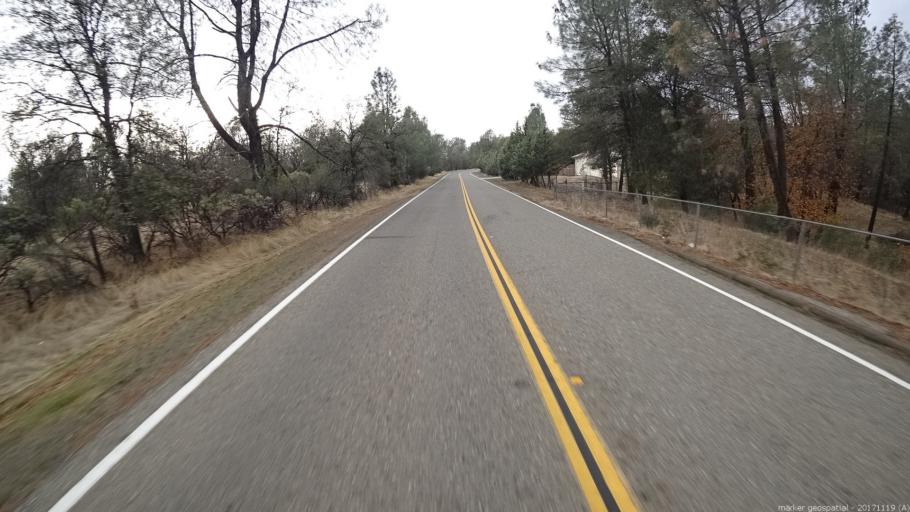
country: US
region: California
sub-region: Shasta County
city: Redding
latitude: 40.4866
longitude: -122.4187
